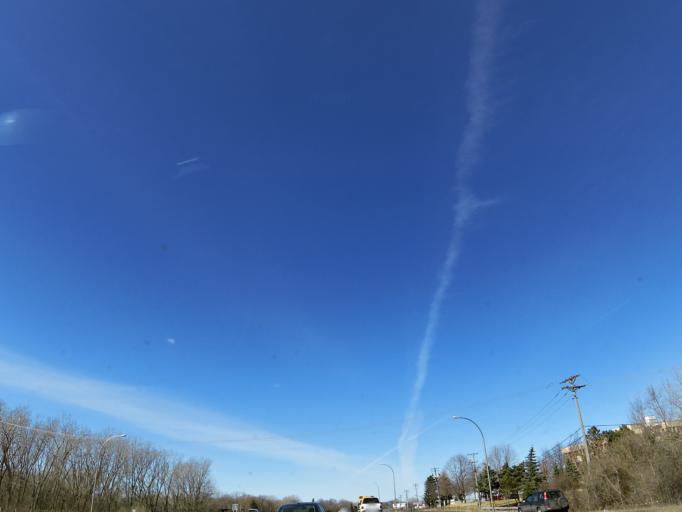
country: US
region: Minnesota
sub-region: Hennepin County
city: Minnetonka Mills
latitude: 44.9836
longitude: -93.4045
